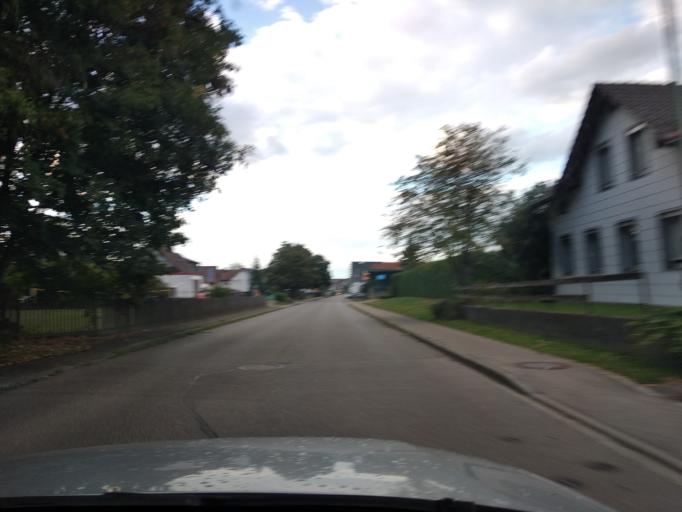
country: DE
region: Bavaria
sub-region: Swabia
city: Woringen
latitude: 47.9191
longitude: 10.2026
